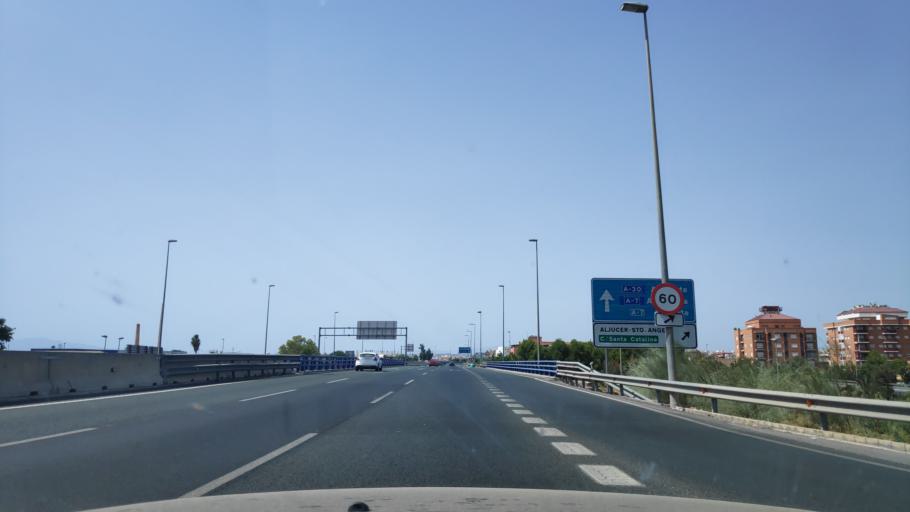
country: ES
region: Murcia
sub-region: Murcia
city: Murcia
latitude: 37.9658
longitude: -1.1365
